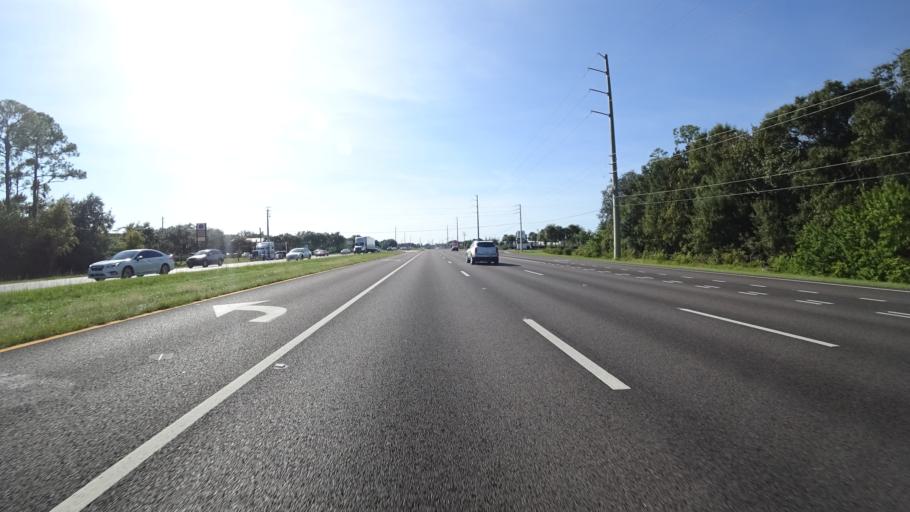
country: US
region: Florida
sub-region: Manatee County
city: Samoset
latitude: 27.4454
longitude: -82.4806
